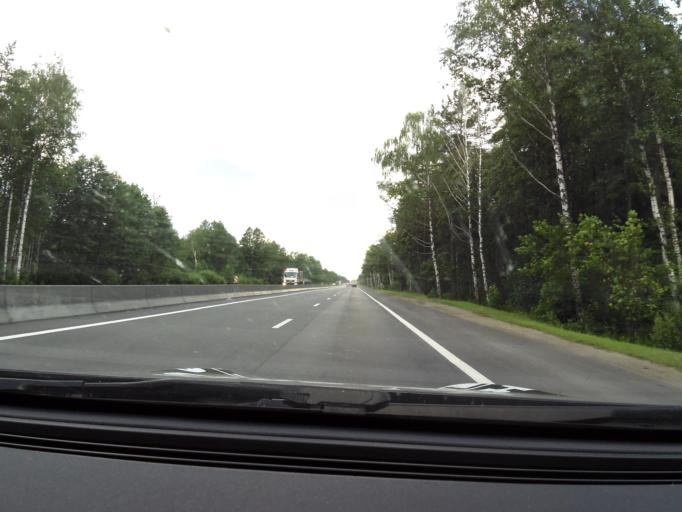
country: RU
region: Nizjnij Novgorod
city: Yuganets
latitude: 56.2888
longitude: 43.2470
